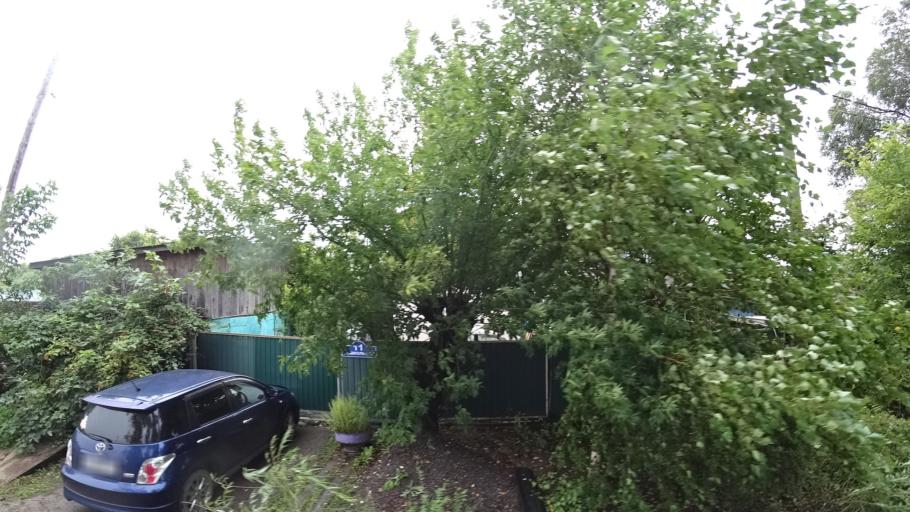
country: RU
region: Primorskiy
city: Monastyrishche
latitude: 44.1980
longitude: 132.4237
